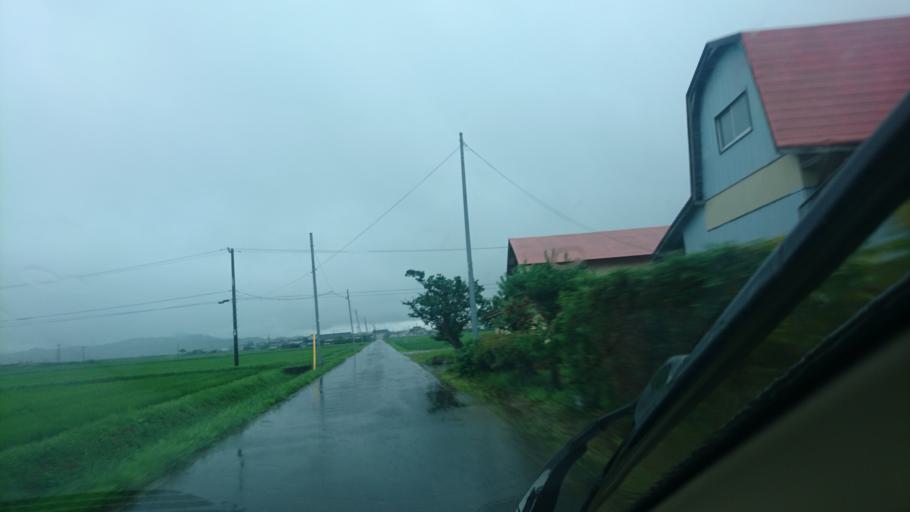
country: JP
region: Iwate
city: Mizusawa
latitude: 39.1772
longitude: 141.1813
